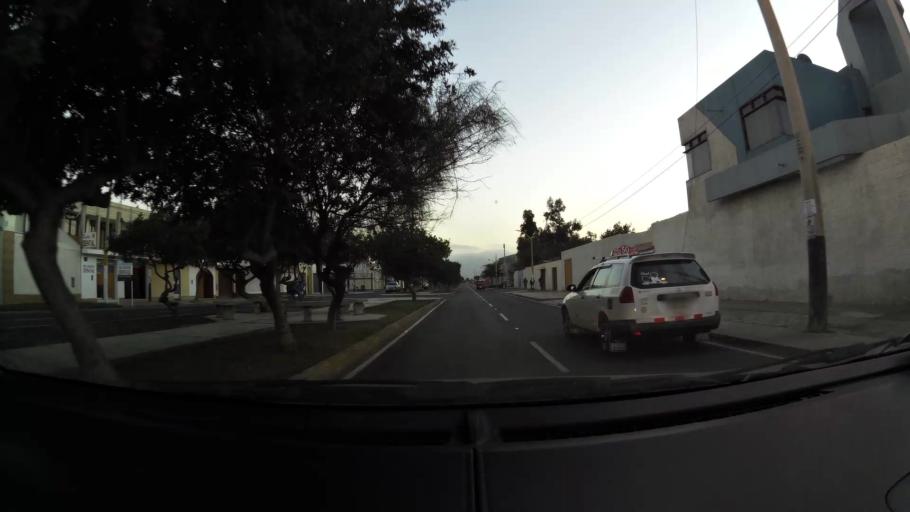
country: PE
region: Ancash
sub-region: Provincia de Santa
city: Buenos Aires
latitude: -9.1241
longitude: -78.5314
